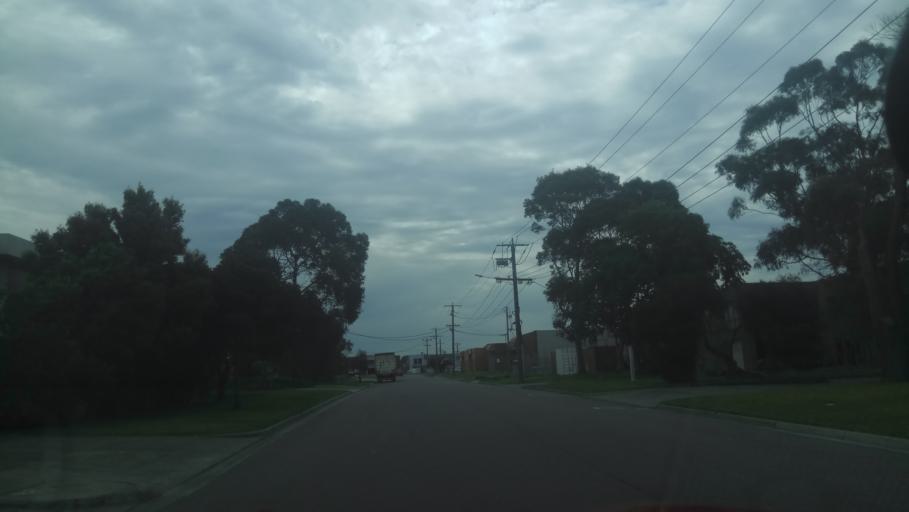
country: AU
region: Victoria
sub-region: Kingston
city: Aspendale Gardens
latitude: -38.0074
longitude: 145.1105
